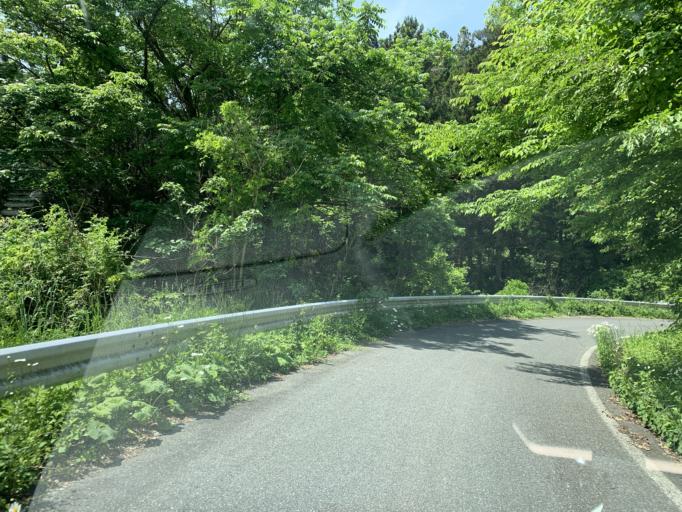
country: JP
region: Iwate
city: Ichinoseki
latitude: 38.9670
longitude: 141.2321
